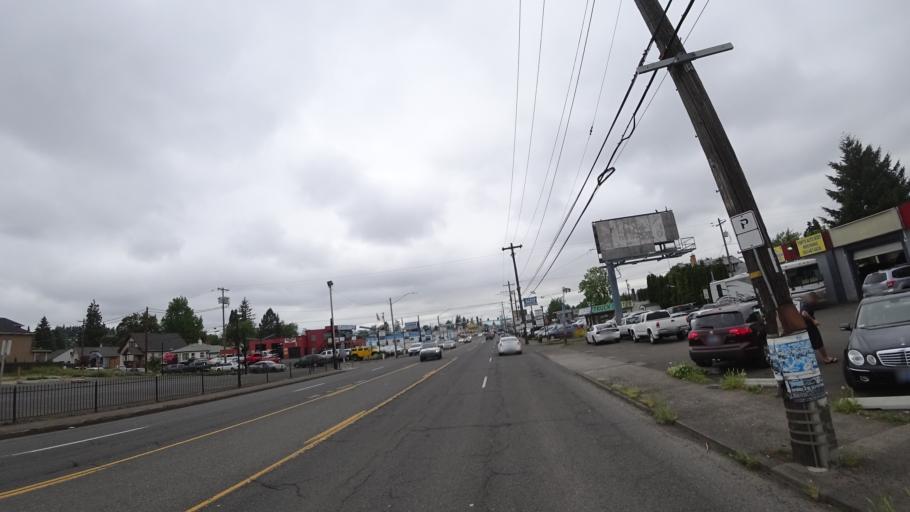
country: US
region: Oregon
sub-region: Multnomah County
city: Lents
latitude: 45.5151
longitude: -122.5788
